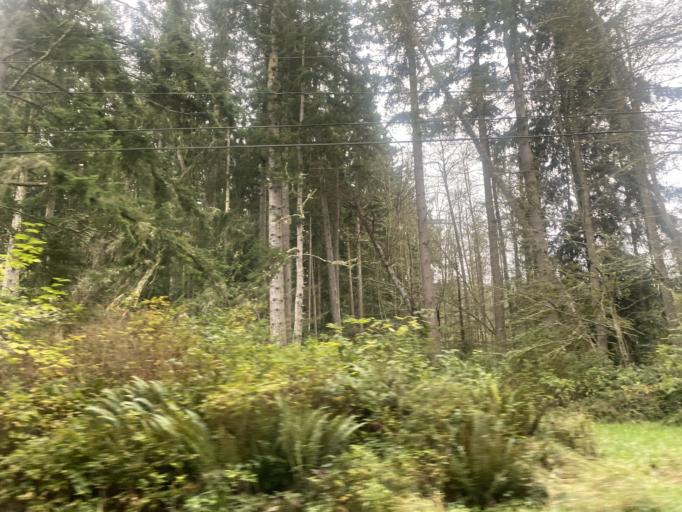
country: US
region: Washington
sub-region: Island County
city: Freeland
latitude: 48.0849
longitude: -122.5664
